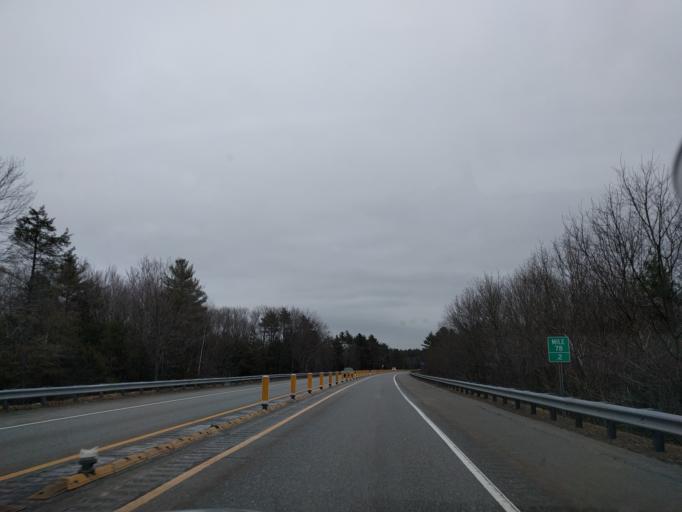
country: US
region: Massachusetts
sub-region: Worcester County
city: Phillipston
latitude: 42.5726
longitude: -72.1452
